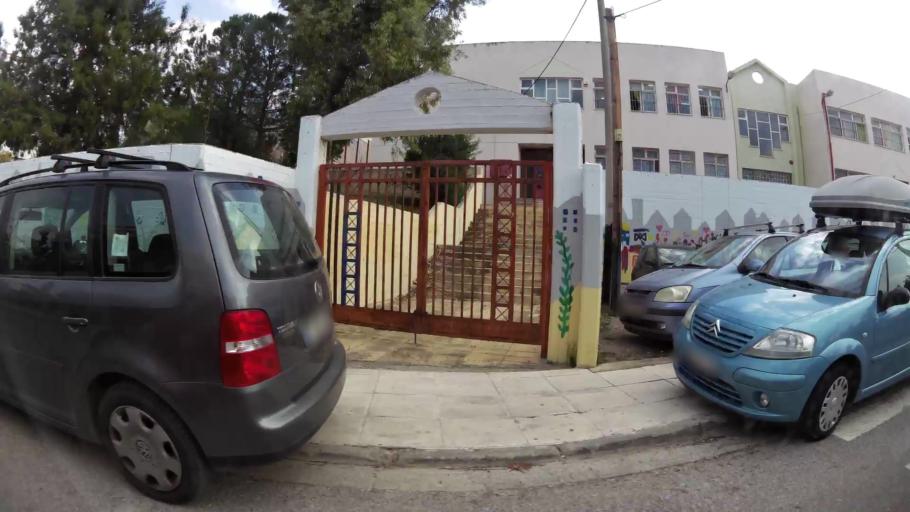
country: GR
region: Attica
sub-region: Nomarchia Dytikis Attikis
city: Zefyri
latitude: 38.0589
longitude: 23.7201
